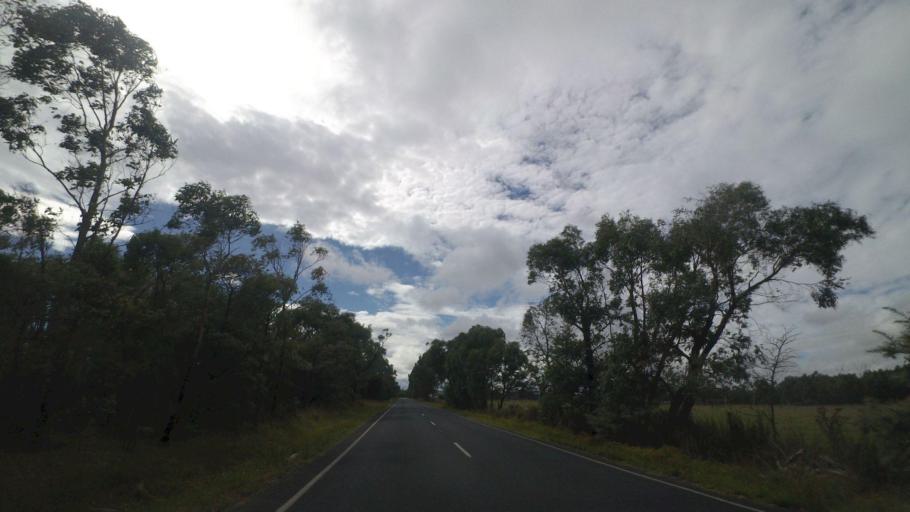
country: AU
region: Victoria
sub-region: Cardinia
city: Bunyip
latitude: -38.0723
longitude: 145.7908
